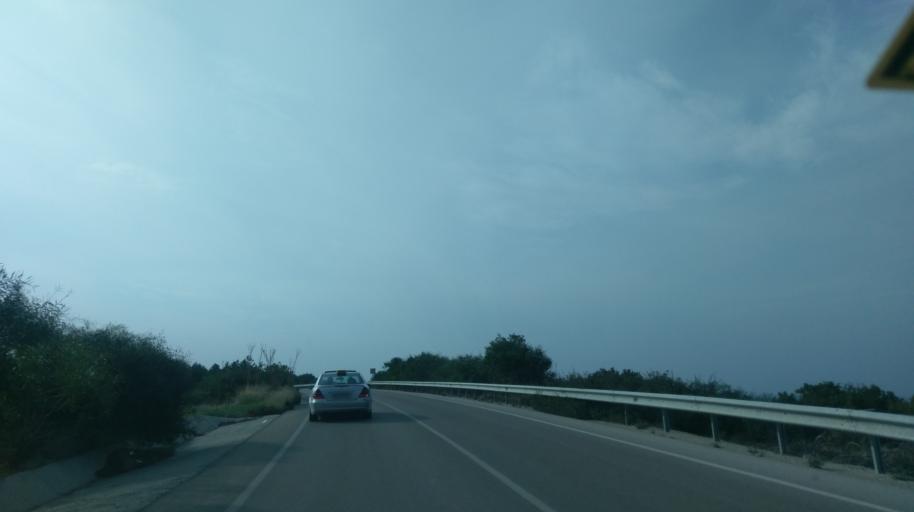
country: CY
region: Ammochostos
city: Trikomo
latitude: 35.4111
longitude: 33.8049
